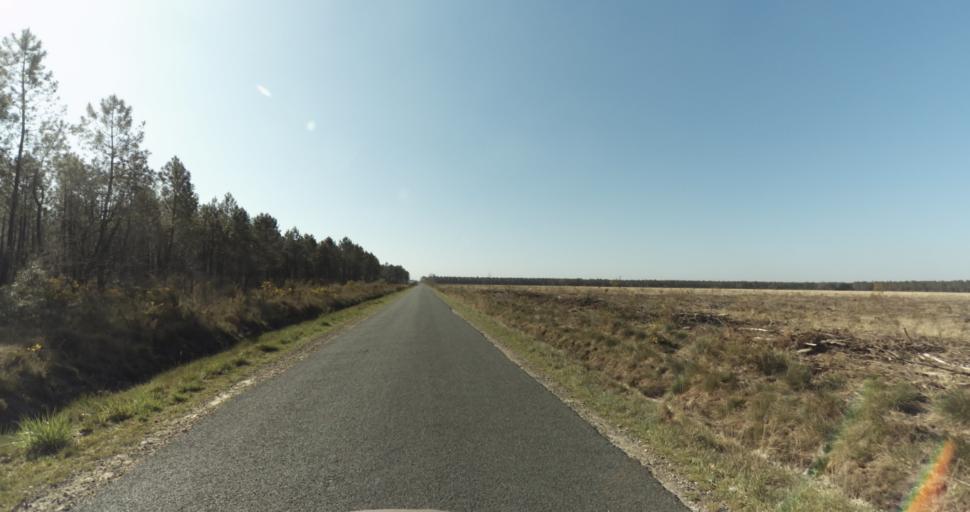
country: FR
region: Aquitaine
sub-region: Departement de la Gironde
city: Marcheprime
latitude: 44.7824
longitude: -0.8612
